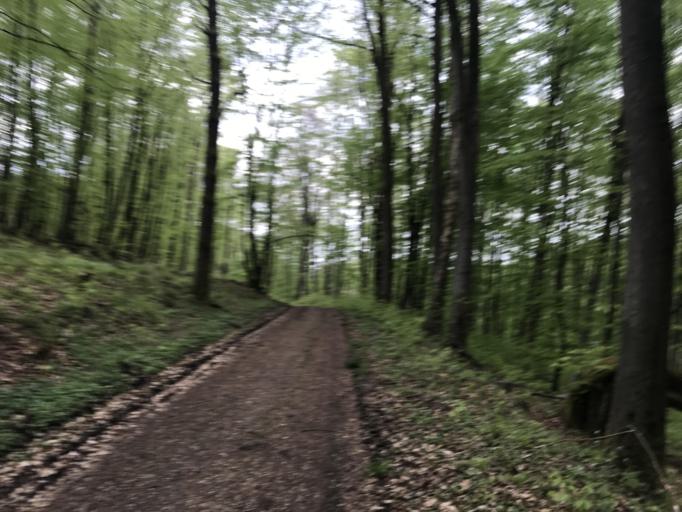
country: DE
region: Hesse
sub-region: Regierungsbezirk Giessen
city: Laubach
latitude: 50.5180
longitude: 8.9899
